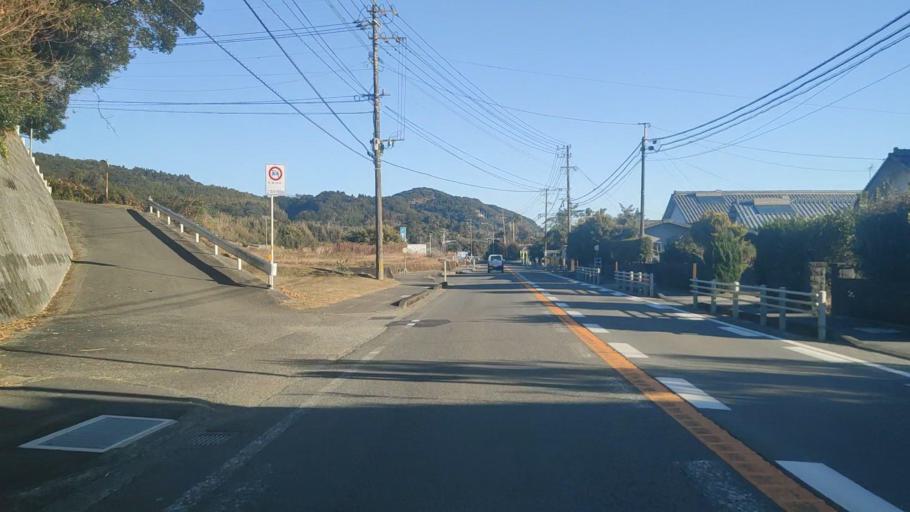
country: JP
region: Miyazaki
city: Nobeoka
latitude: 32.3607
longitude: 131.6221
